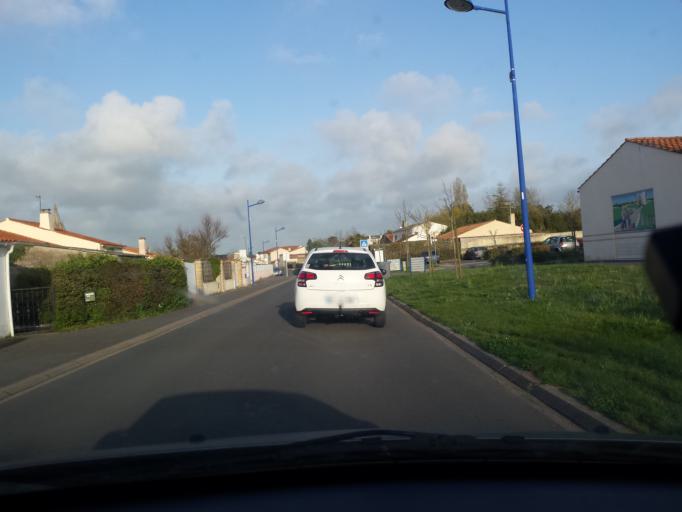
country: FR
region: Pays de la Loire
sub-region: Departement de la Vendee
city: Saint-Mathurin
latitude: 46.5644
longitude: -1.7177
